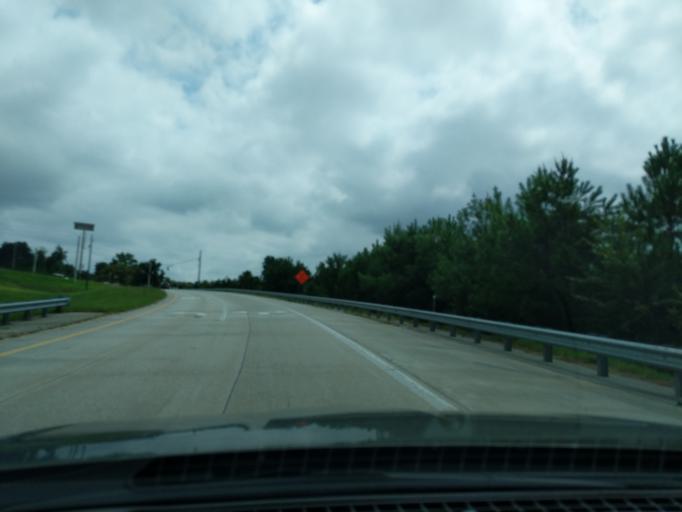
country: US
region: Georgia
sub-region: Columbia County
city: Grovetown
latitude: 33.4830
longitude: -82.2010
